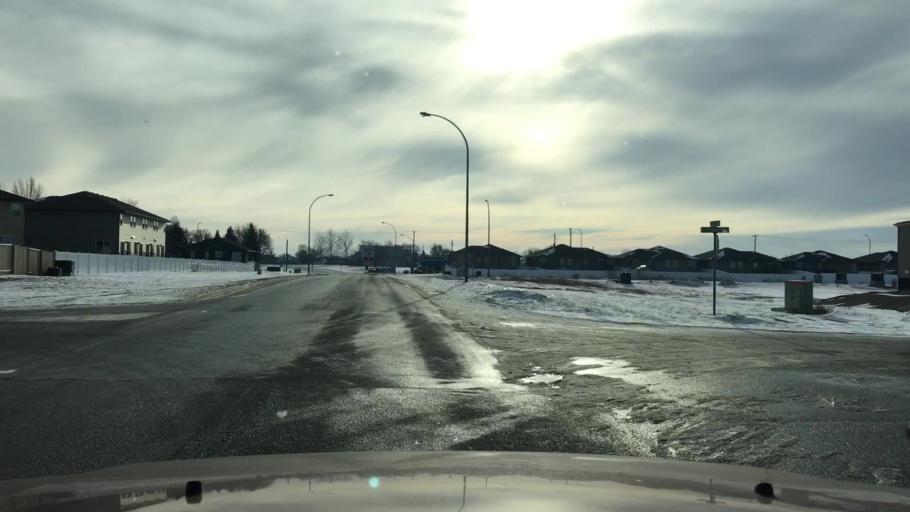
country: CA
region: Saskatchewan
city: Pilot Butte
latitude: 50.4861
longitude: -104.4202
